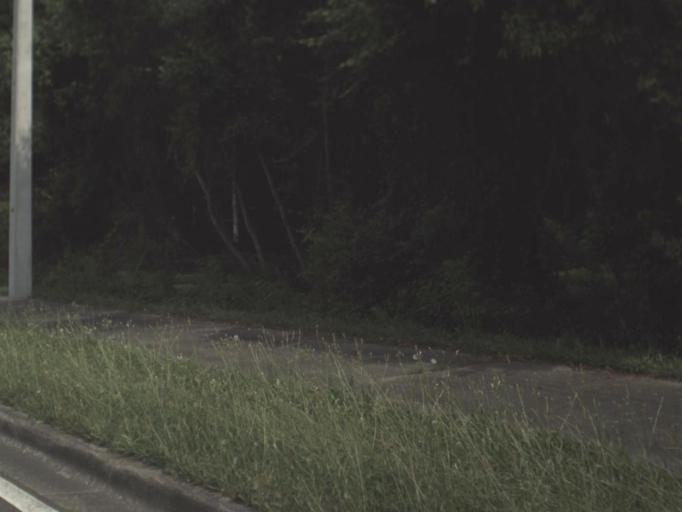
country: US
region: Florida
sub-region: Clay County
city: Bellair-Meadowbrook Terrace
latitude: 30.2470
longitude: -81.8377
